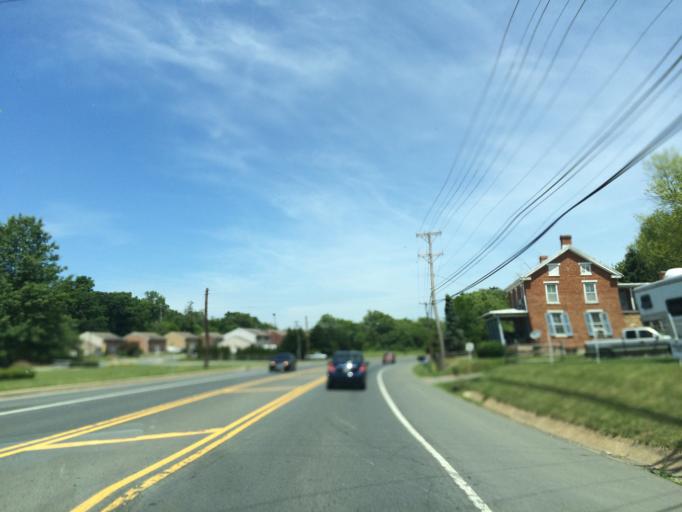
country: US
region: Maryland
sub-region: Washington County
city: Saint James
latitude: 39.5881
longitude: -77.7316
